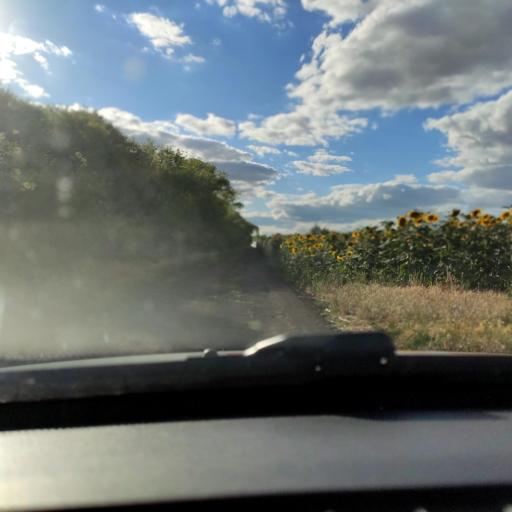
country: RU
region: Voronezj
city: Verkhnyaya Khava
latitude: 51.5928
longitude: 39.8456
